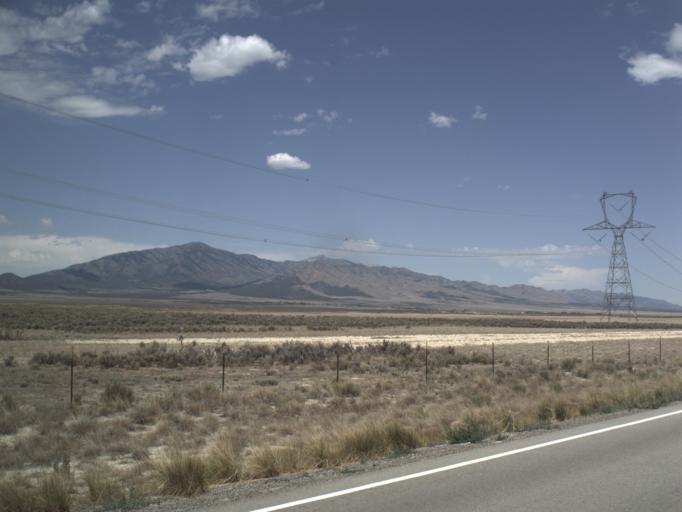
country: US
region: Utah
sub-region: Tooele County
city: Tooele
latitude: 40.2694
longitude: -112.3975
